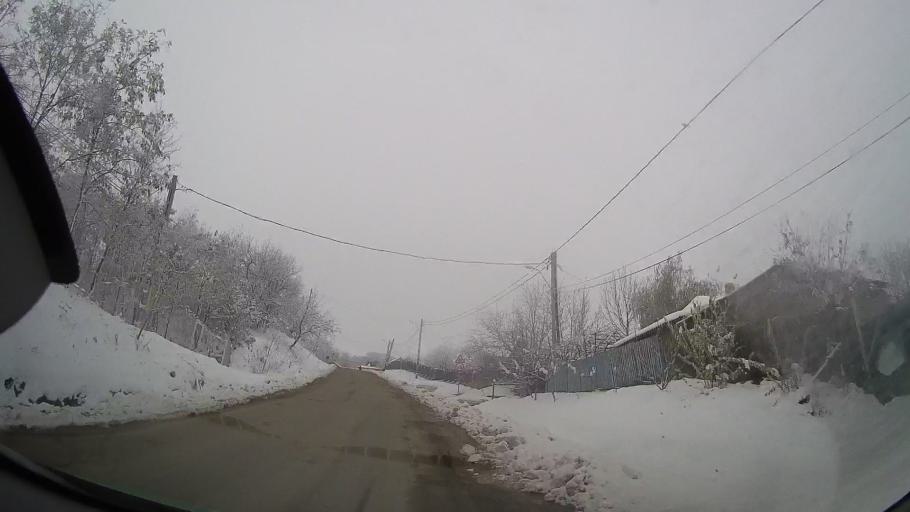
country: RO
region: Iasi
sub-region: Comuna Tibanesti
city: Tibanesti
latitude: 46.8963
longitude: 27.3176
